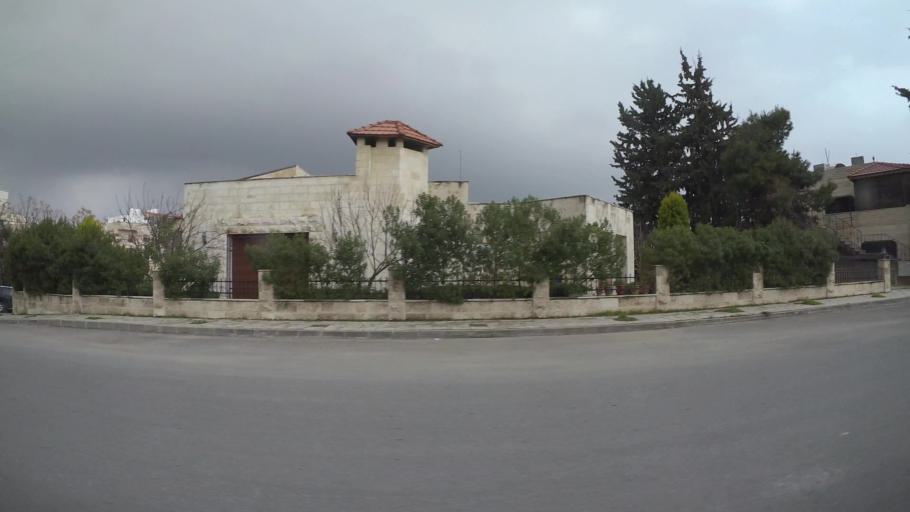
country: JO
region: Amman
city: Umm as Summaq
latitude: 31.8864
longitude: 35.8545
